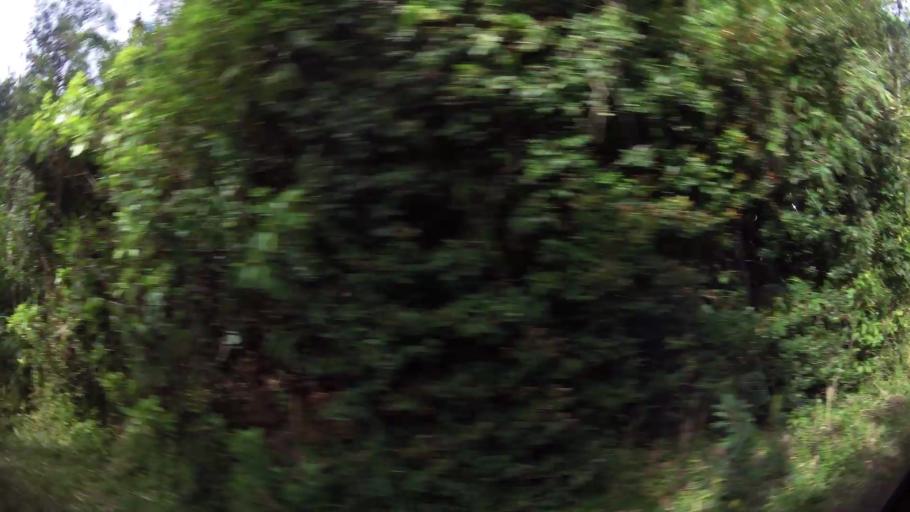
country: ZA
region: Western Cape
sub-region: Eden District Municipality
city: Knysna
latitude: -34.0617
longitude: 23.0837
